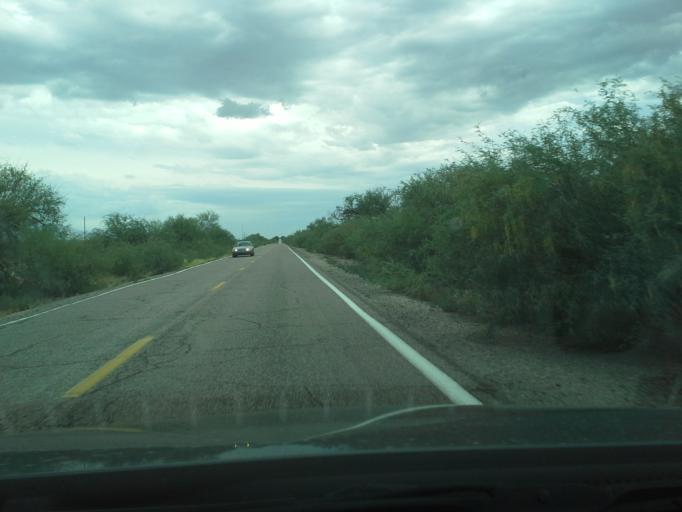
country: US
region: Arizona
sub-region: Pima County
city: Marana
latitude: 32.4751
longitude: -111.2336
